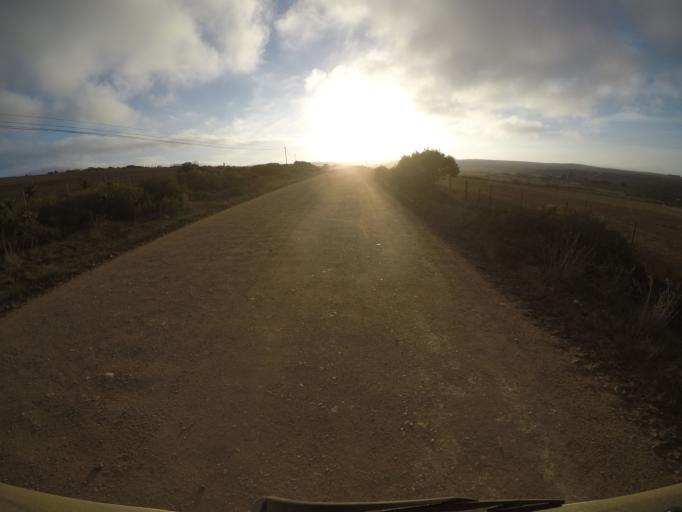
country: ZA
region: Western Cape
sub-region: Eden District Municipality
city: Mossel Bay
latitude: -34.1086
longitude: 22.0641
